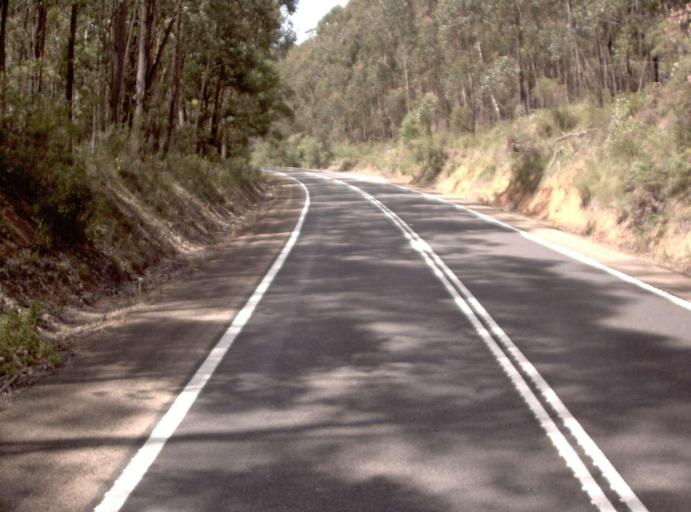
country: AU
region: New South Wales
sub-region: Bombala
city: Bombala
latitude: -37.5485
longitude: 149.3633
